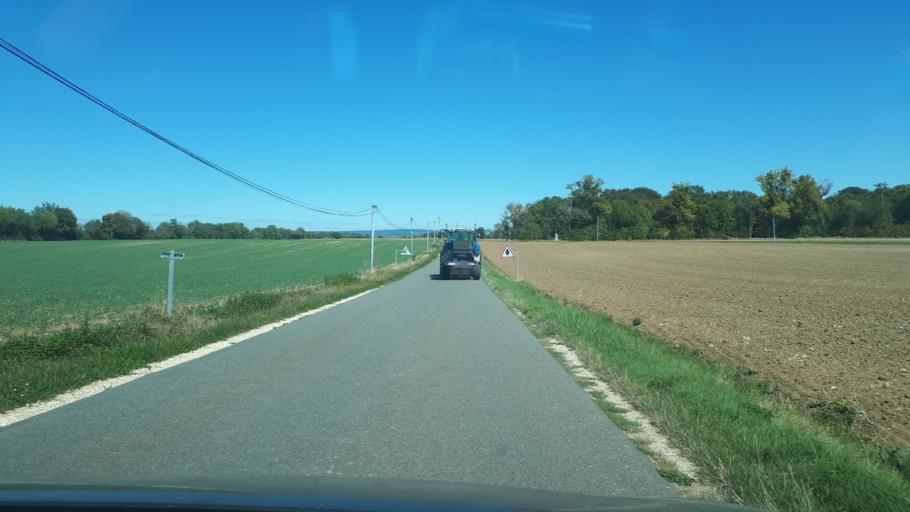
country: FR
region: Centre
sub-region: Departement du Cher
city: Sainte-Solange
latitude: 47.1467
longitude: 2.5592
